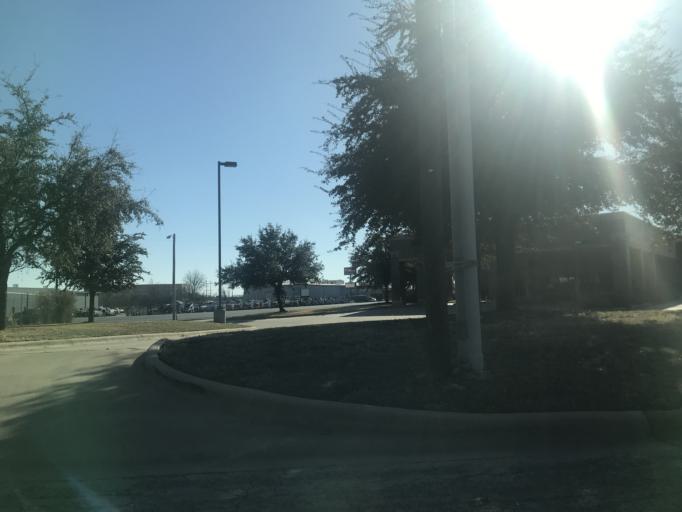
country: US
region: Texas
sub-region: Taylor County
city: Abilene
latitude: 32.4231
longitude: -99.7363
